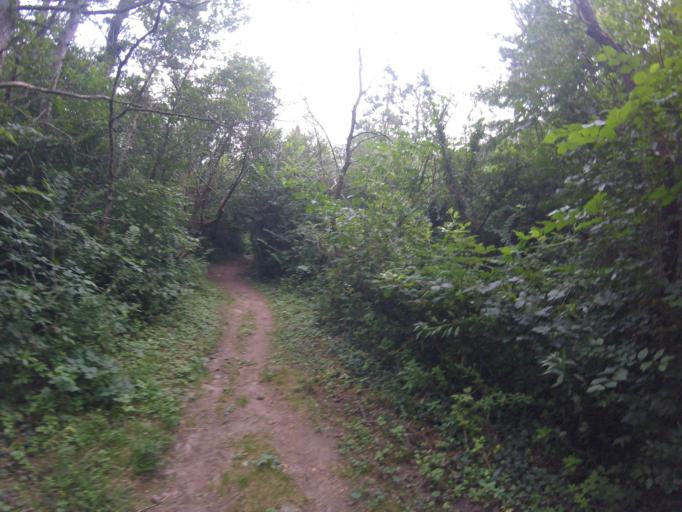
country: HU
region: Veszprem
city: Tapolca
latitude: 46.8449
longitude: 17.4498
